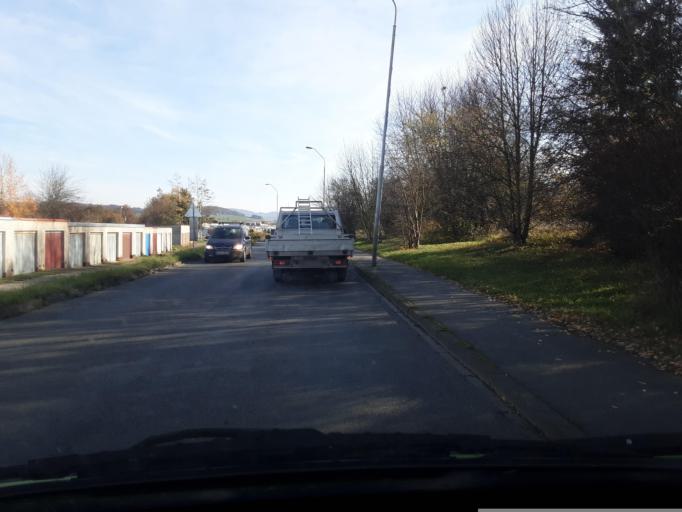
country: CZ
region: Plzensky
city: Klatovy
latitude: 49.3875
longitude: 13.2909
